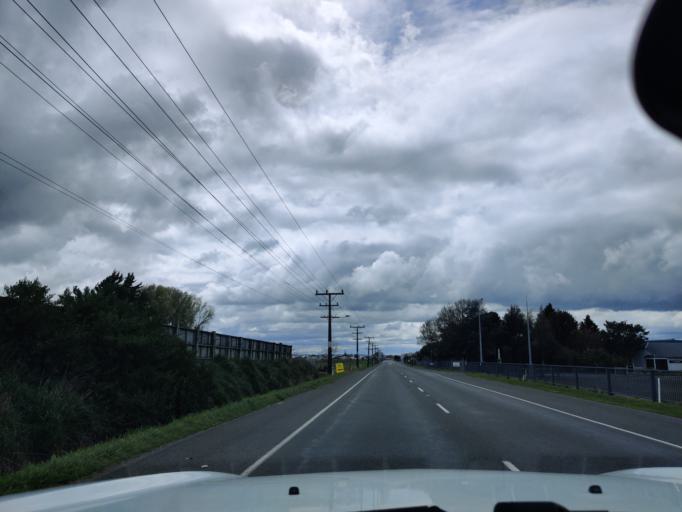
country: NZ
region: Manawatu-Wanganui
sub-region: Palmerston North City
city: Palmerston North
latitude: -40.2384
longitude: 175.5620
